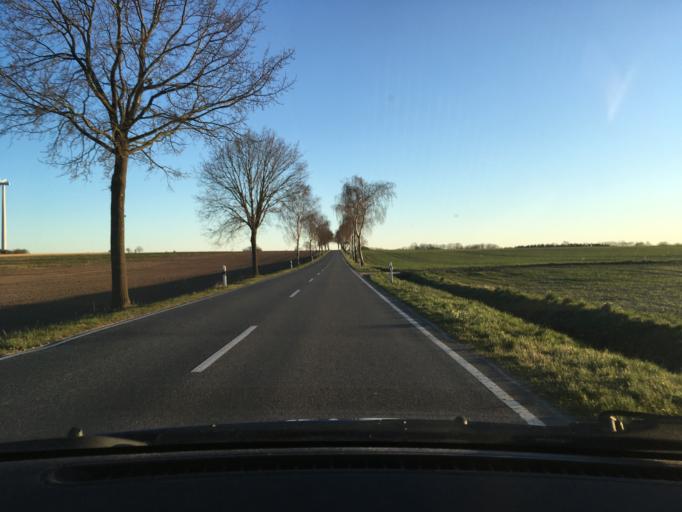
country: DE
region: Lower Saxony
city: Dahlem
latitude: 53.2122
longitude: 10.7549
